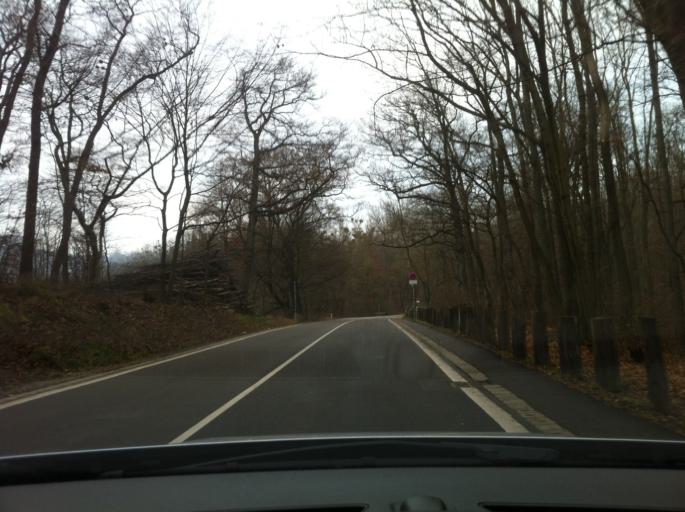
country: AT
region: Lower Austria
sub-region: Politischer Bezirk Wien-Umgebung
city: Klosterneuburg
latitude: 48.2412
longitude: 16.2741
